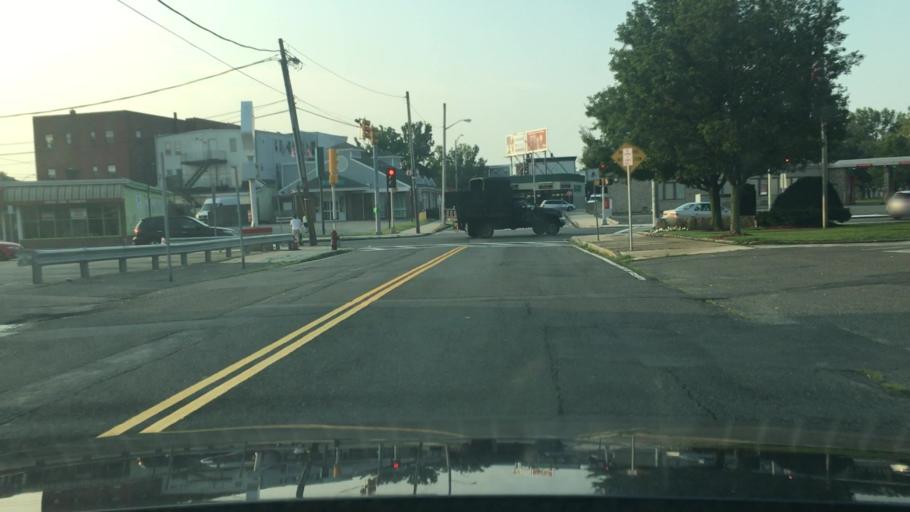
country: US
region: Massachusetts
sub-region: Essex County
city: Lynn
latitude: 42.4637
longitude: -70.9650
